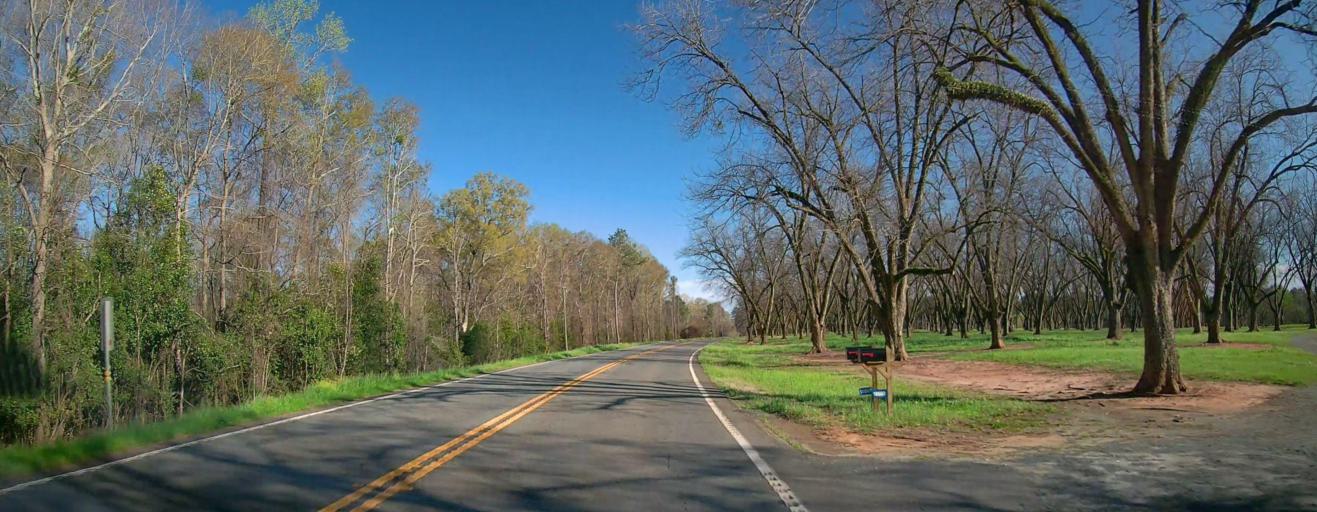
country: US
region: Georgia
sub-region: Macon County
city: Marshallville
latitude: 32.4542
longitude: -83.9138
